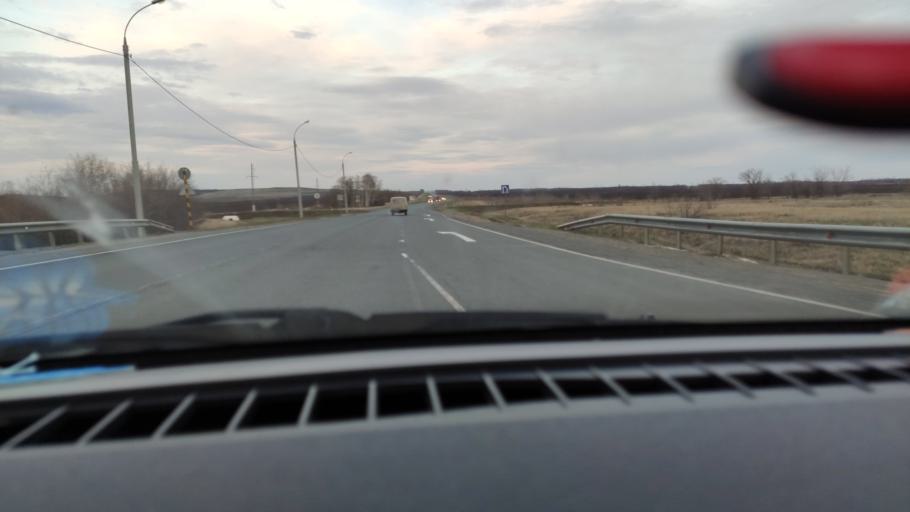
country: RU
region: Saratov
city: Yelshanka
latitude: 51.8298
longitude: 46.2444
